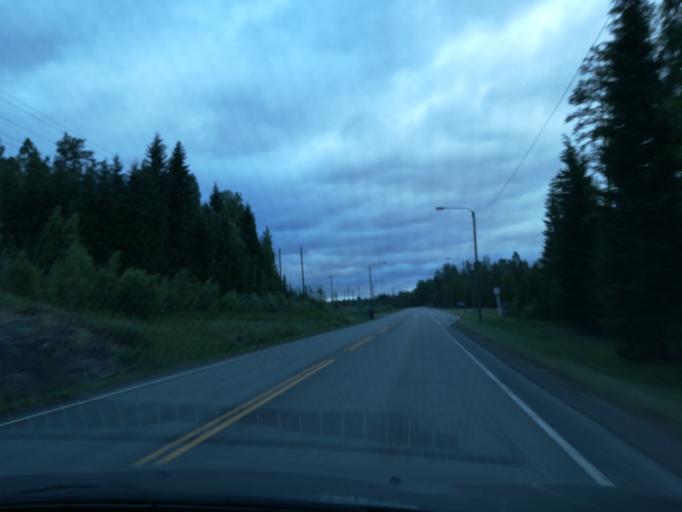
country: FI
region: Southern Savonia
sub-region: Mikkeli
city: Ristiina
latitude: 61.4696
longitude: 27.2550
